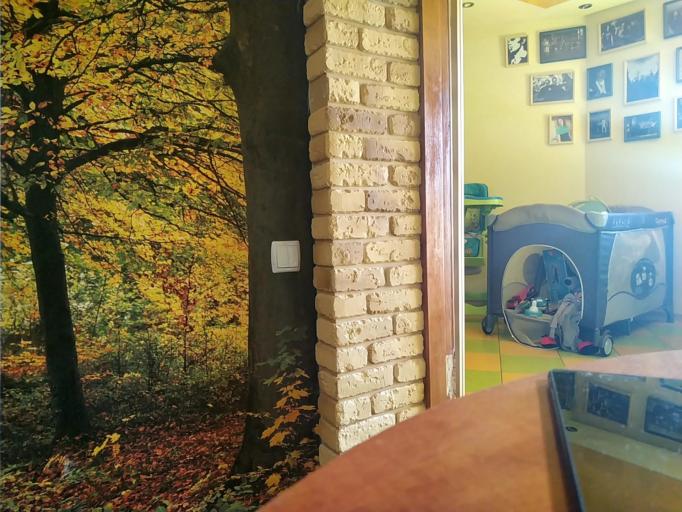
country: RU
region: Tverskaya
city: Vydropuzhsk
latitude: 57.4678
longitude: 34.7039
